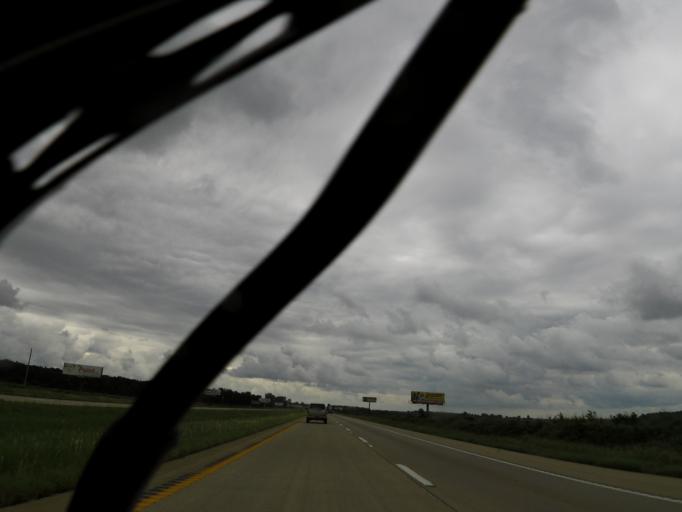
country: US
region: Missouri
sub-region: Mississippi County
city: Charleston
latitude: 36.9260
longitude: -89.3127
